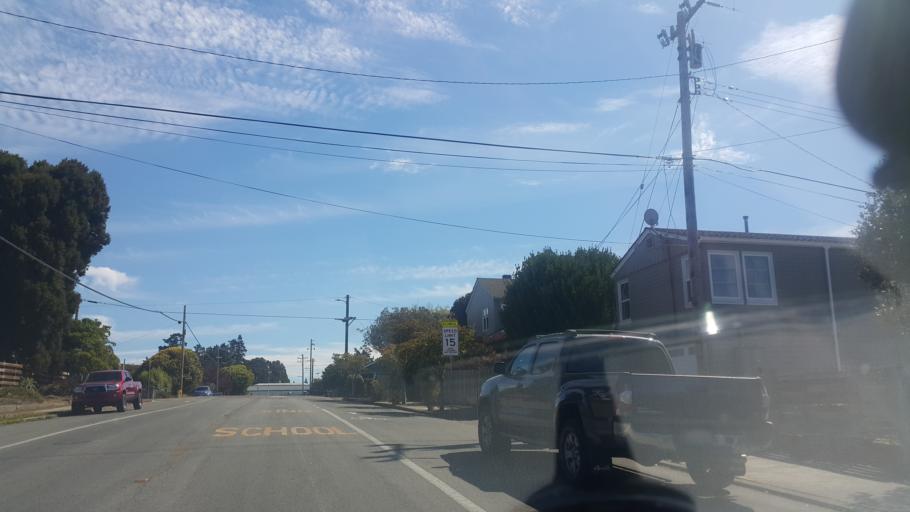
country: US
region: California
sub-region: Mendocino County
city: Fort Bragg
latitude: 39.4479
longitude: -123.8005
